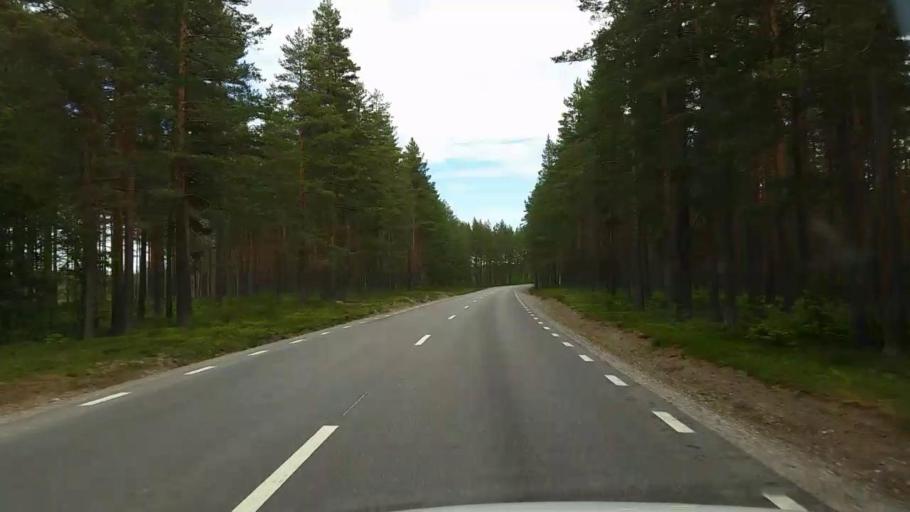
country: SE
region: Gaevleborg
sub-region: Sandvikens Kommun
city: Jarbo
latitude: 60.9503
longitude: 16.3943
